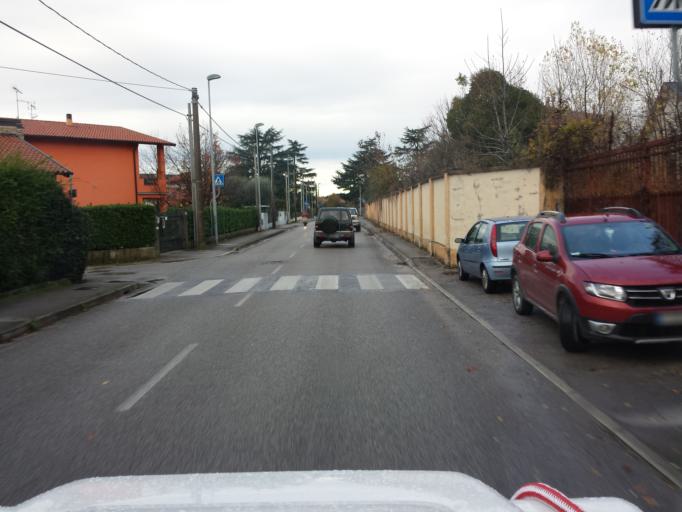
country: IT
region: Friuli Venezia Giulia
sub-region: Provincia di Gorizia
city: Gradisca d'Isonzo
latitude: 45.8911
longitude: 13.4927
